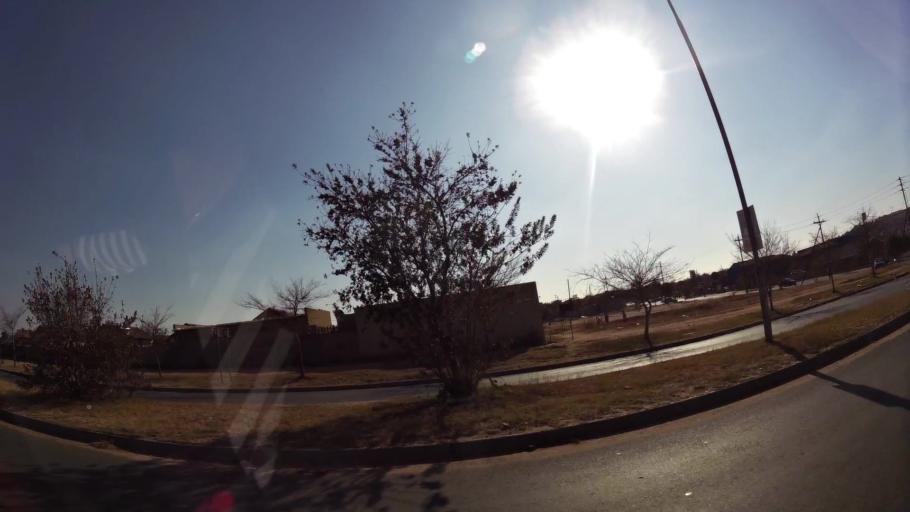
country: ZA
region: Gauteng
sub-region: West Rand District Municipality
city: Muldersdriseloop
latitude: -26.0416
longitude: 27.9138
